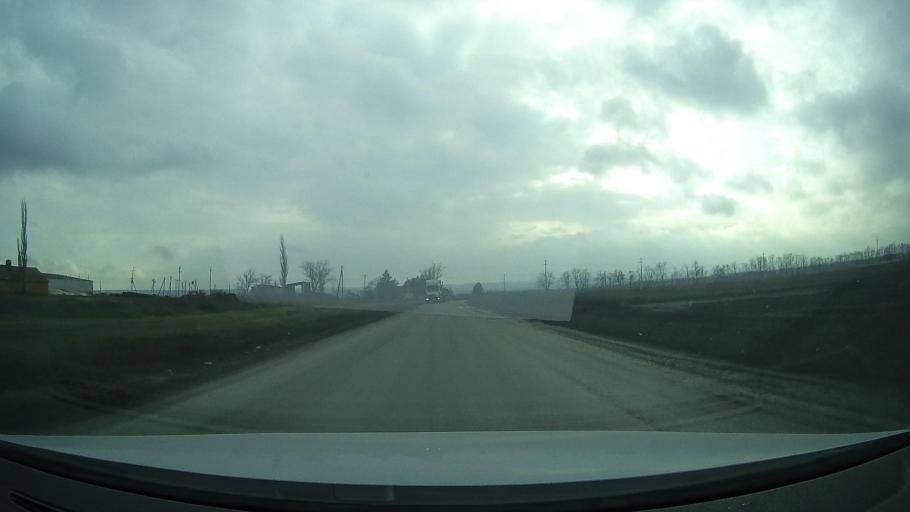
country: RU
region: Rostov
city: Grushevskaya
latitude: 47.4812
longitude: 39.9284
